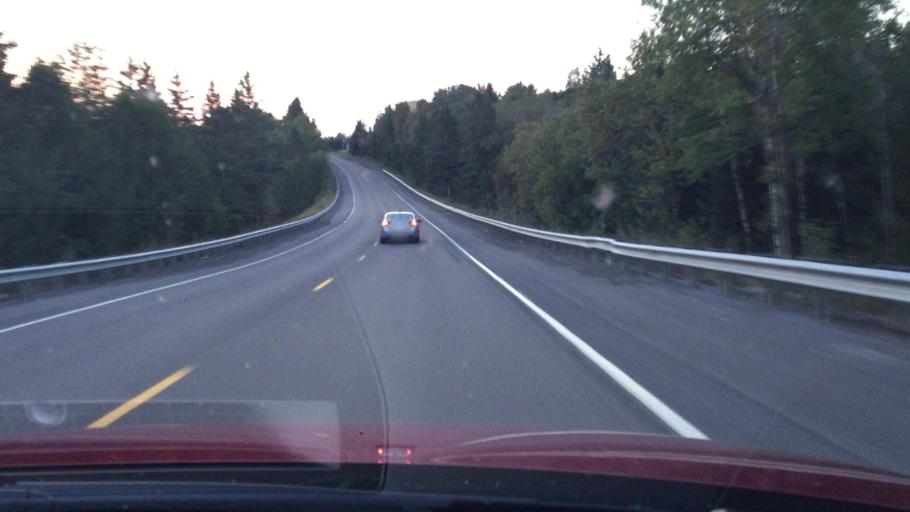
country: US
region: Maine
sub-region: Aroostook County
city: Easton
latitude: 46.5984
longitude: -67.9671
